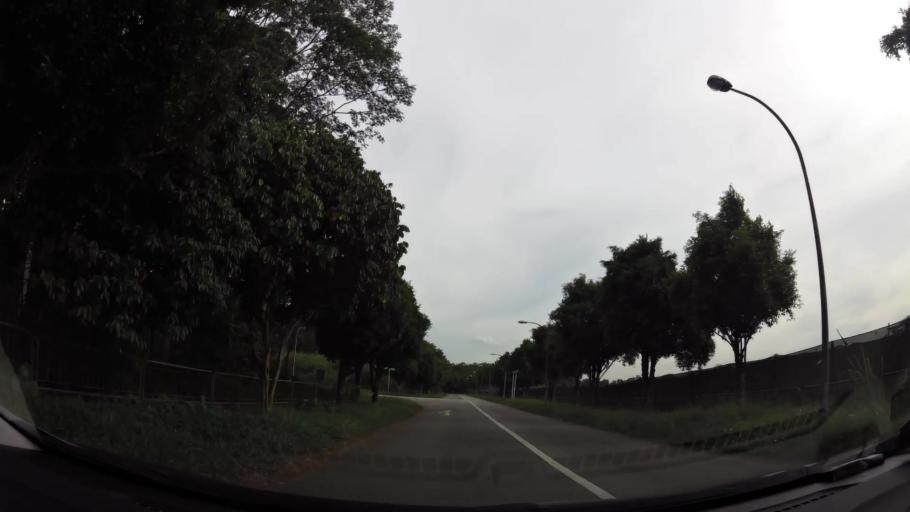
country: MY
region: Johor
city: Johor Bahru
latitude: 1.4412
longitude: 103.7141
